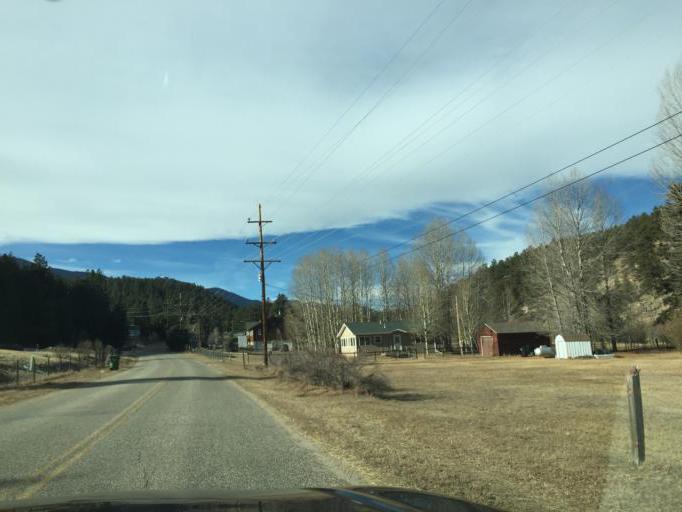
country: US
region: Colorado
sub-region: Jefferson County
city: Evergreen
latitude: 39.4061
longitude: -105.4831
